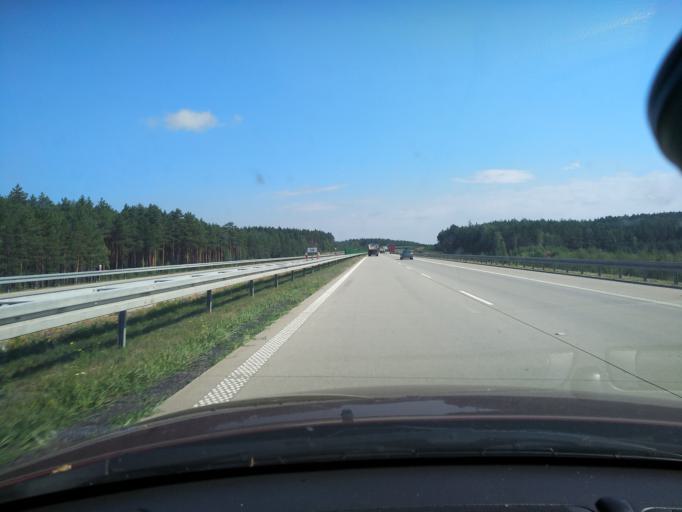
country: PL
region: Lower Silesian Voivodeship
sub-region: Powiat boleslawiecki
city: Nowogrodziec
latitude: 51.2597
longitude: 15.3616
